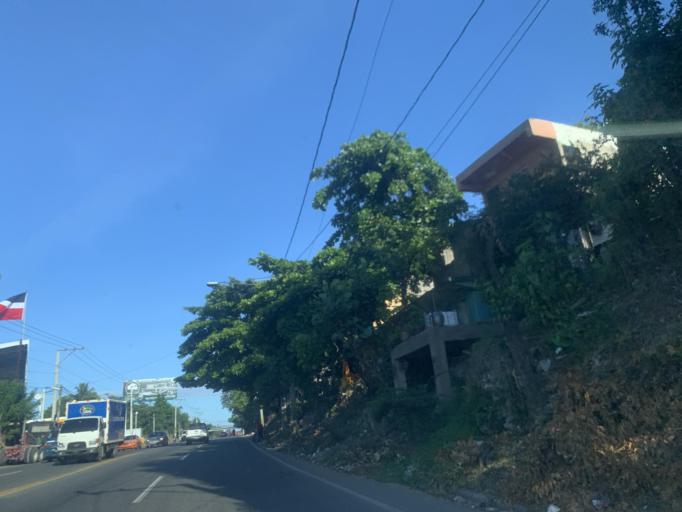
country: DO
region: San Cristobal
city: El Carril
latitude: 18.4351
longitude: -70.0124
